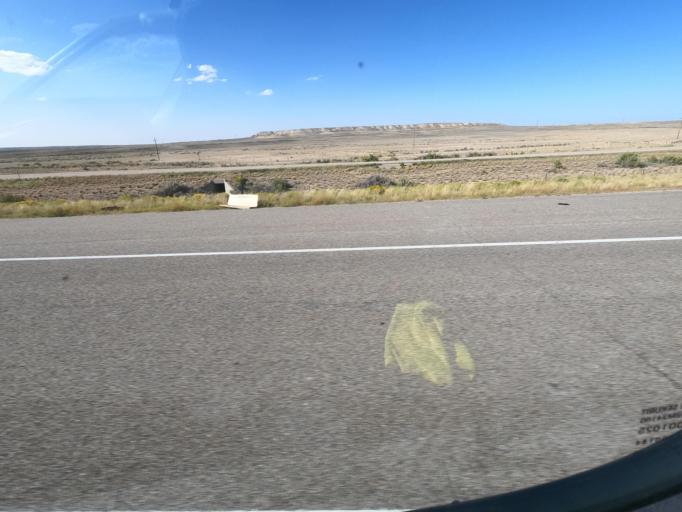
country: US
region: Wyoming
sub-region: Sweetwater County
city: Green River
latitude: 41.5431
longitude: -109.7982
